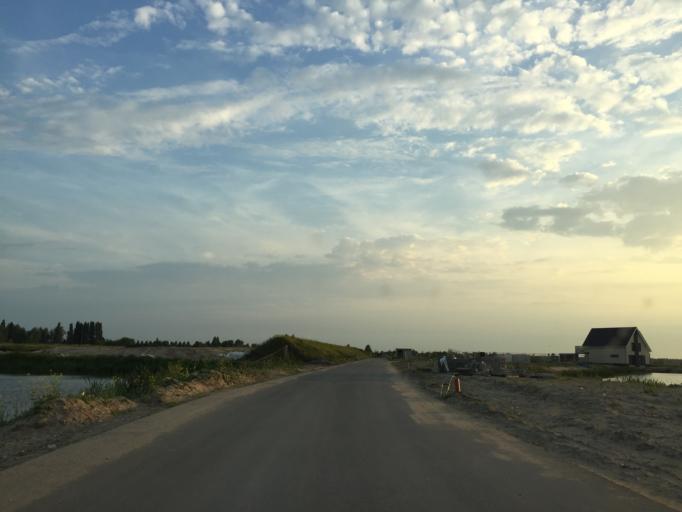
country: NL
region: South Holland
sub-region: Gemeente Gouda
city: Gouda
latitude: 52.0012
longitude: 4.6869
